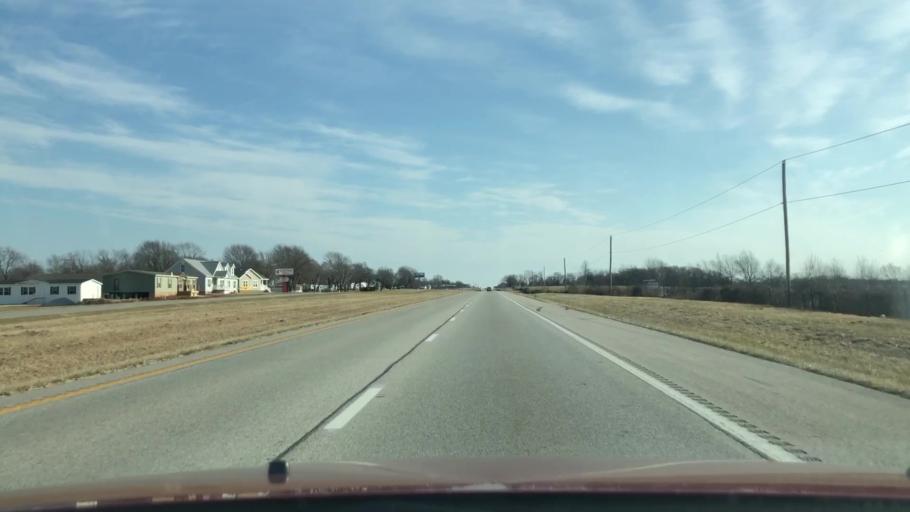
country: US
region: Missouri
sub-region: Webster County
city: Rogersville
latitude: 37.1187
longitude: -93.1341
